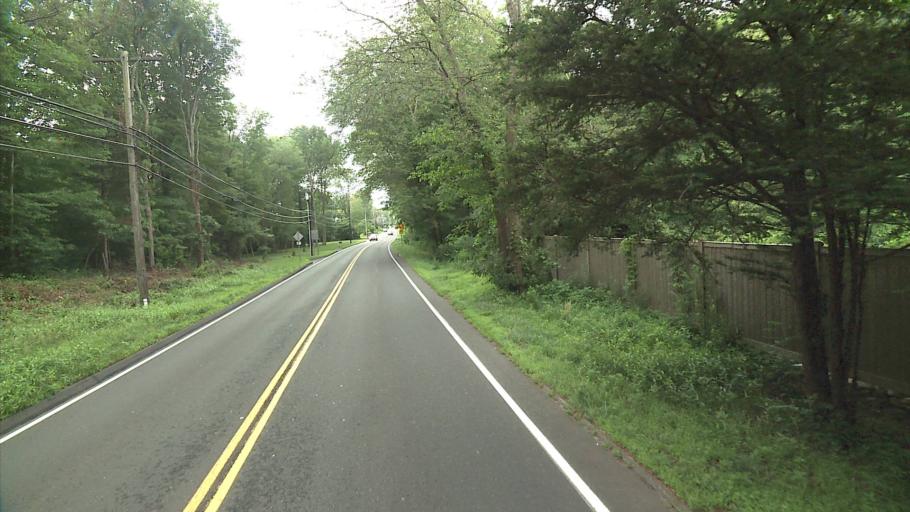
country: US
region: Connecticut
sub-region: New Haven County
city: Madison
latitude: 41.3620
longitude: -72.5660
